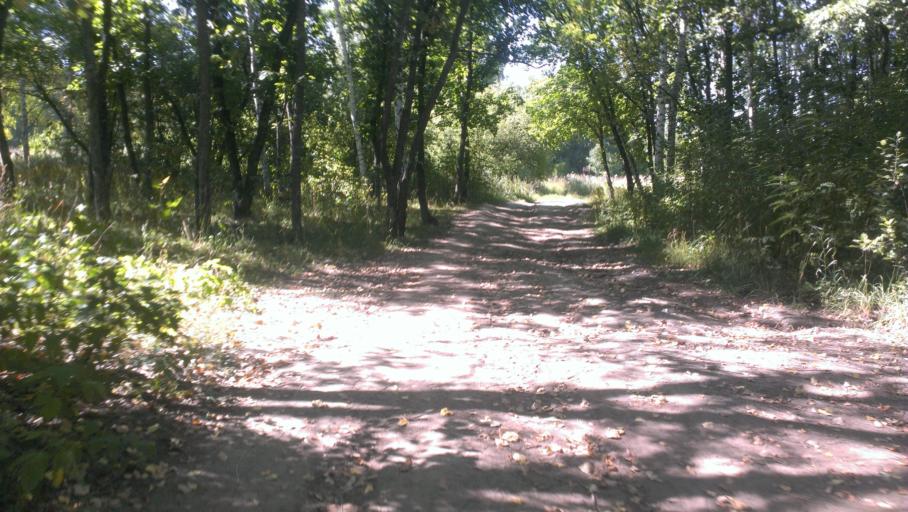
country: RU
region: Altai Krai
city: Nauchnyy Gorodok
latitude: 53.4233
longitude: 83.5112
